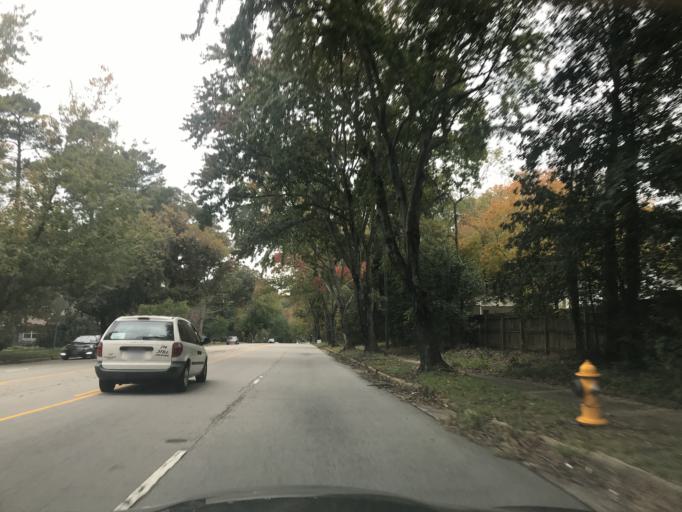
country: US
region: North Carolina
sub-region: Wake County
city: West Raleigh
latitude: 35.8508
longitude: -78.6176
